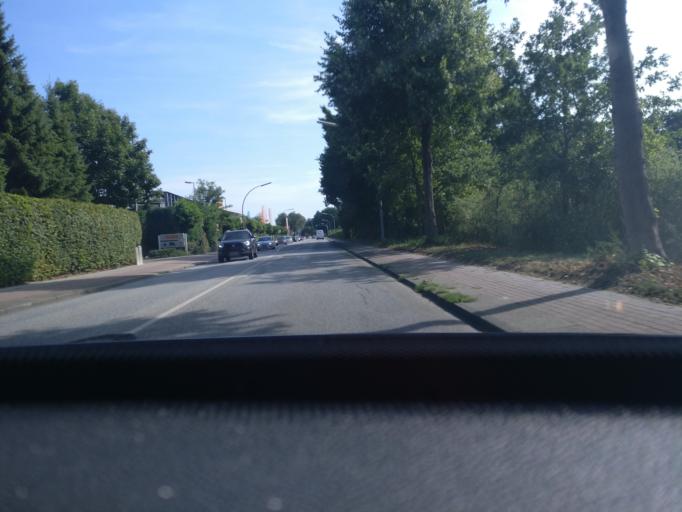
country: DE
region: Schleswig-Holstein
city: Norderstedt
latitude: 53.6698
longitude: 9.9702
